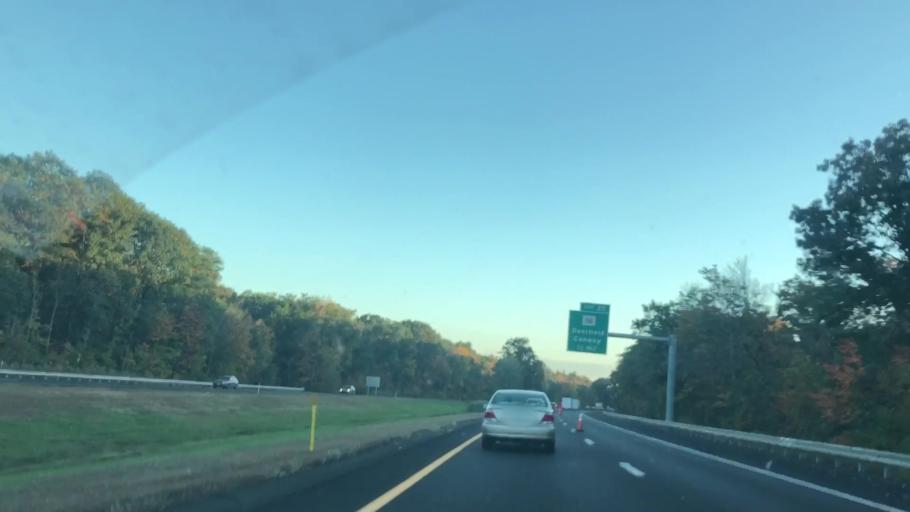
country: US
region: Massachusetts
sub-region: Franklin County
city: South Deerfield
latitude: 42.4939
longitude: -72.6169
